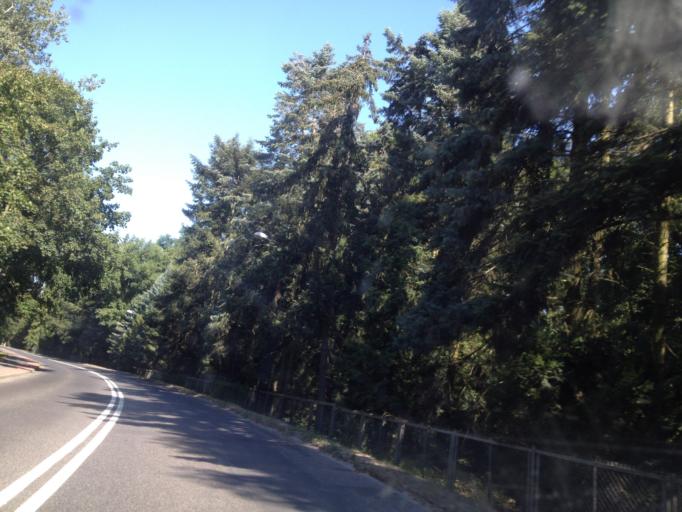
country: PL
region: Greater Poland Voivodeship
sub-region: Powiat poznanski
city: Kornik
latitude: 52.2378
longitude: 17.0929
